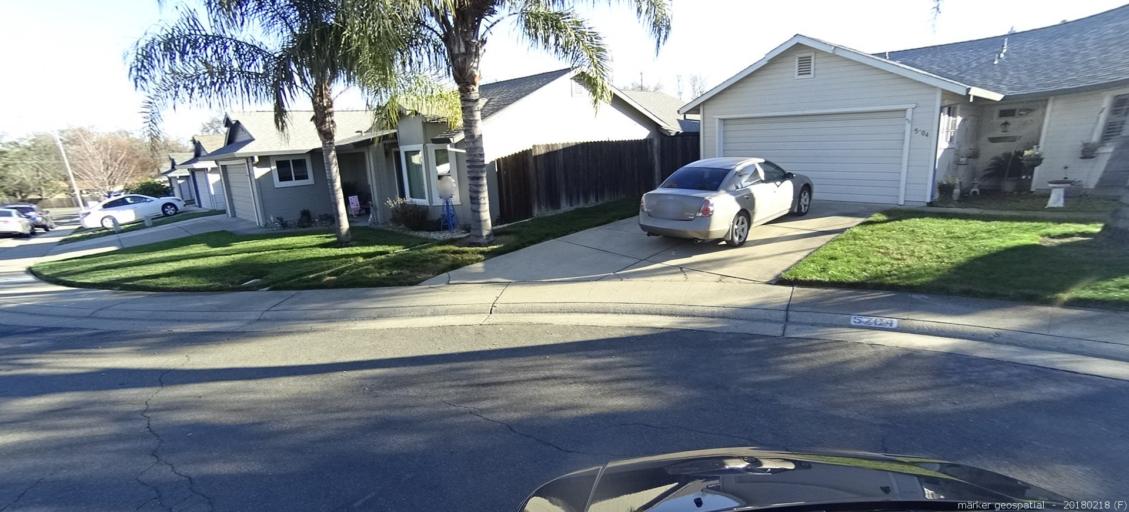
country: US
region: California
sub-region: Sacramento County
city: Orangevale
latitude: 38.6692
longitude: -121.2058
